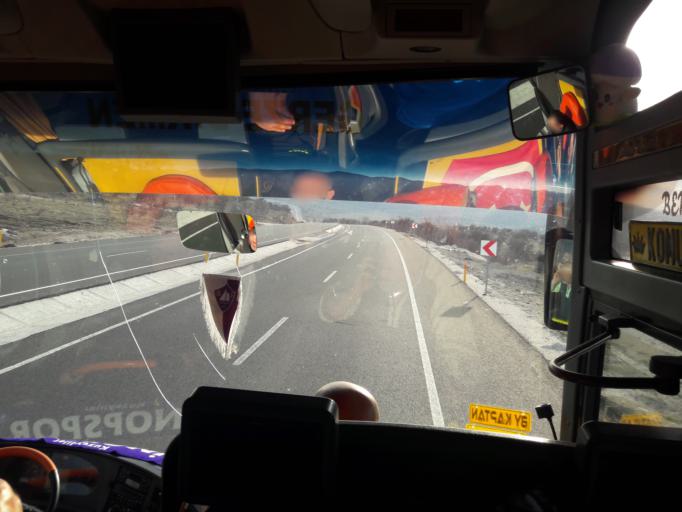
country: TR
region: Cankiri
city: Ilgaz
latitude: 40.8450
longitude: 33.5885
